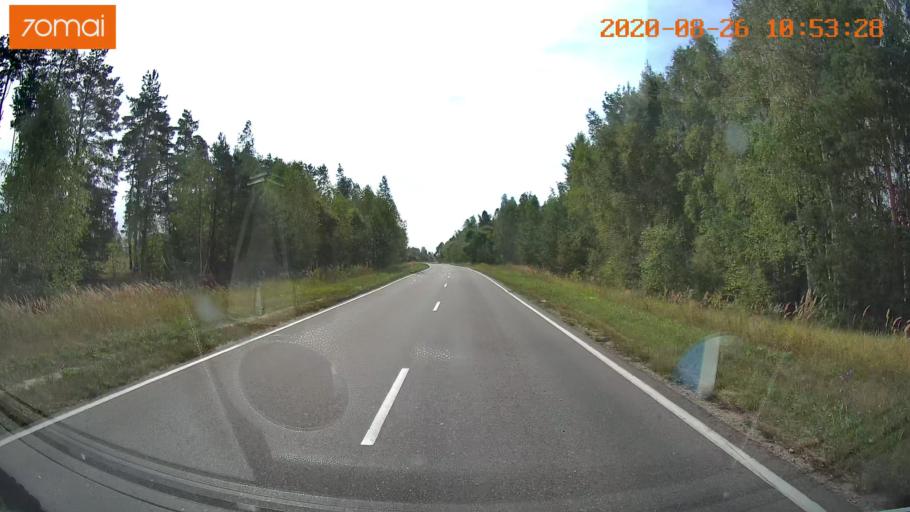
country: RU
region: Rjazan
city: Izhevskoye
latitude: 54.6413
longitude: 41.1518
